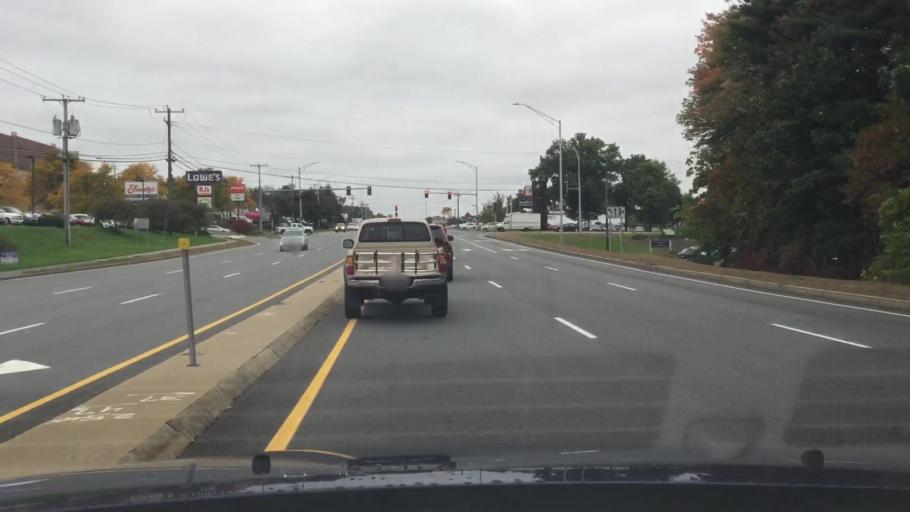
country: US
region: New Hampshire
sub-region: Hillsborough County
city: Hudson
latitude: 42.7248
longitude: -71.4454
